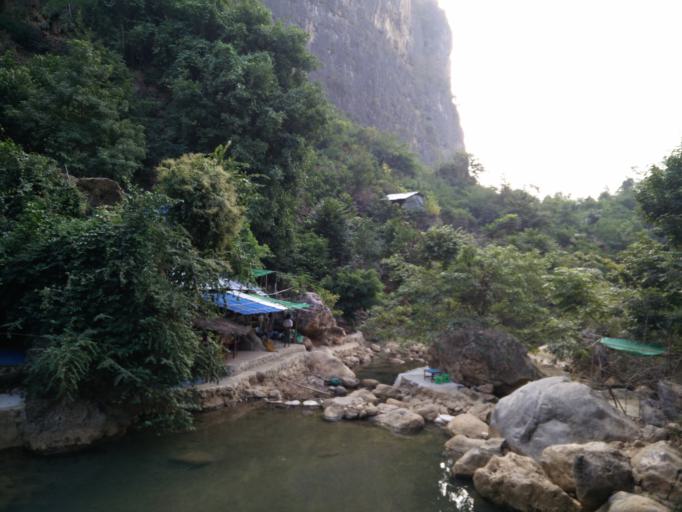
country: MM
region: Mandalay
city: Kyaukse
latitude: 21.7074
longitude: 96.3554
